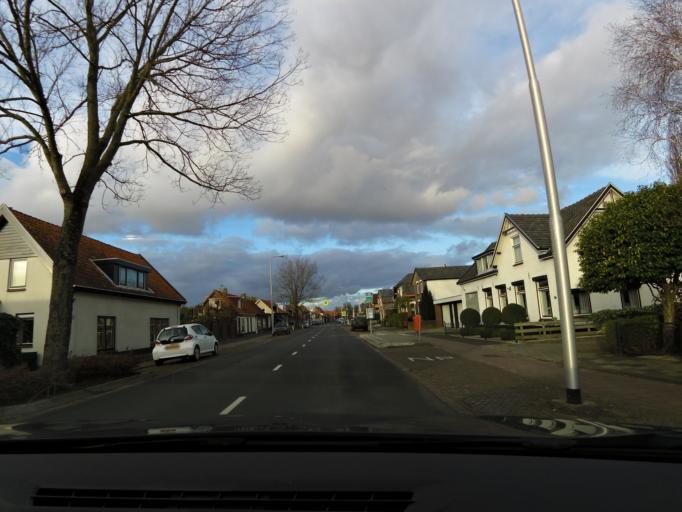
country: NL
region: North Brabant
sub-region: Gemeente Moerdijk
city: Willemstad
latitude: 51.7337
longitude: 4.4386
